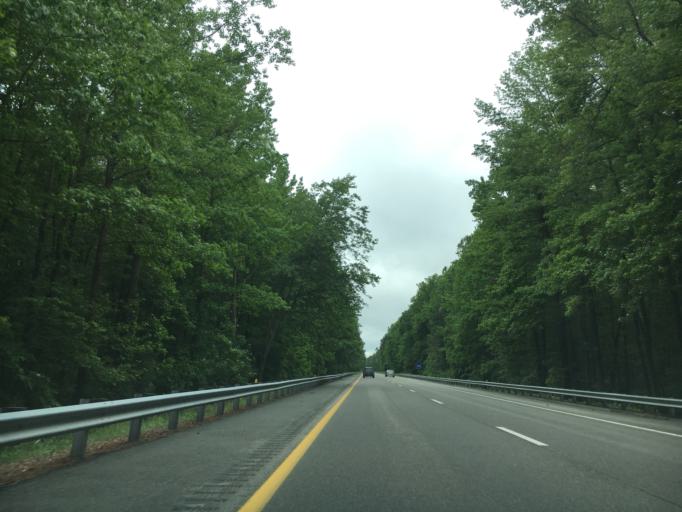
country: US
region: Virginia
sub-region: Brunswick County
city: Lawrenceville
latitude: 36.9113
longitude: -77.7781
